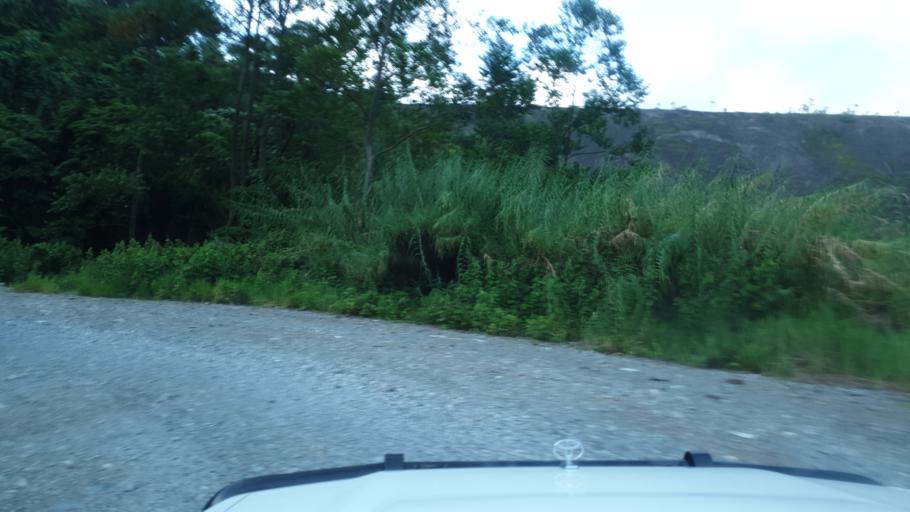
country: PG
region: Bougainville
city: Panguna
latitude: -6.3343
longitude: 155.4648
